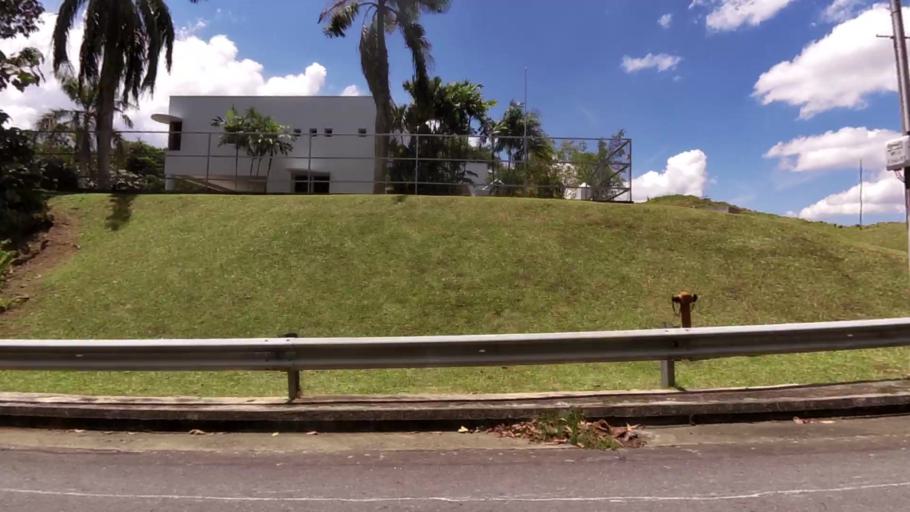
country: BN
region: Brunei and Muara
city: Bandar Seri Begawan
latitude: 4.9289
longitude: 114.9636
